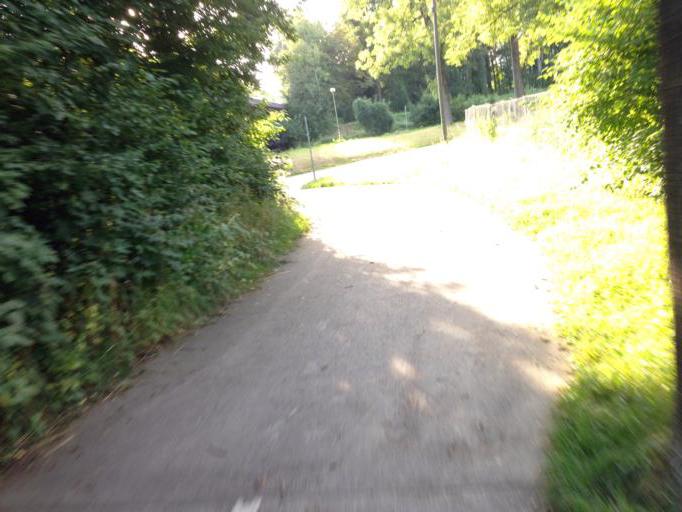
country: DE
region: Bavaria
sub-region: Swabia
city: Stadtbergen
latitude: 48.3489
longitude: 10.8680
